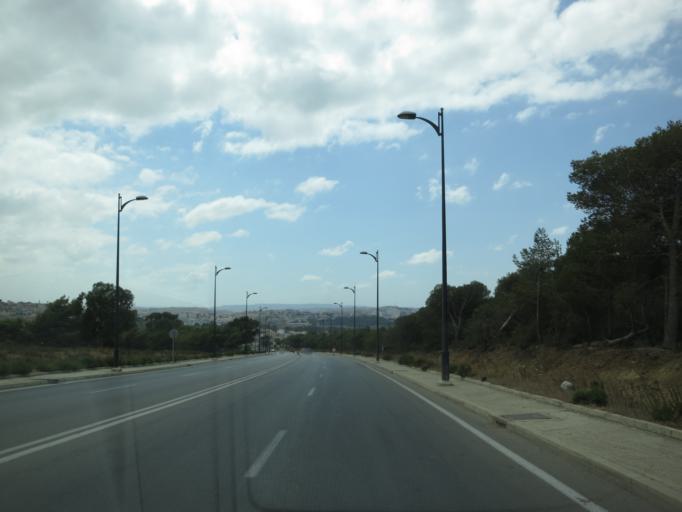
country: MA
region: Tanger-Tetouan
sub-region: Tanger-Assilah
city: Tangier
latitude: 35.7925
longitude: -5.7514
